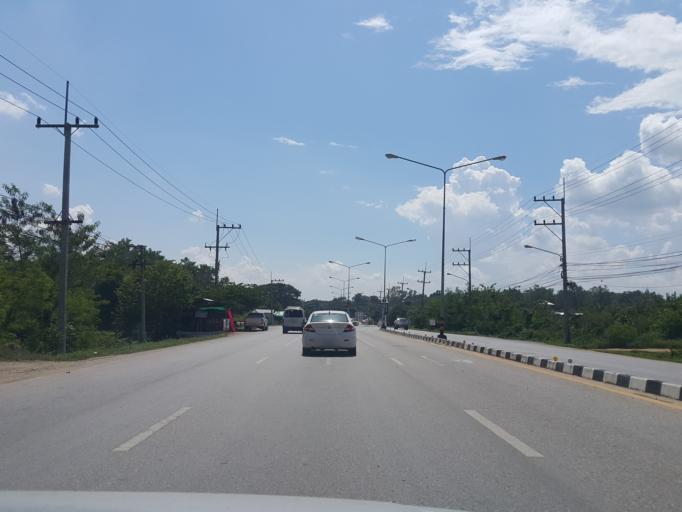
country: TH
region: Chiang Mai
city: Mae Taeng
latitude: 19.0672
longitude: 98.9395
